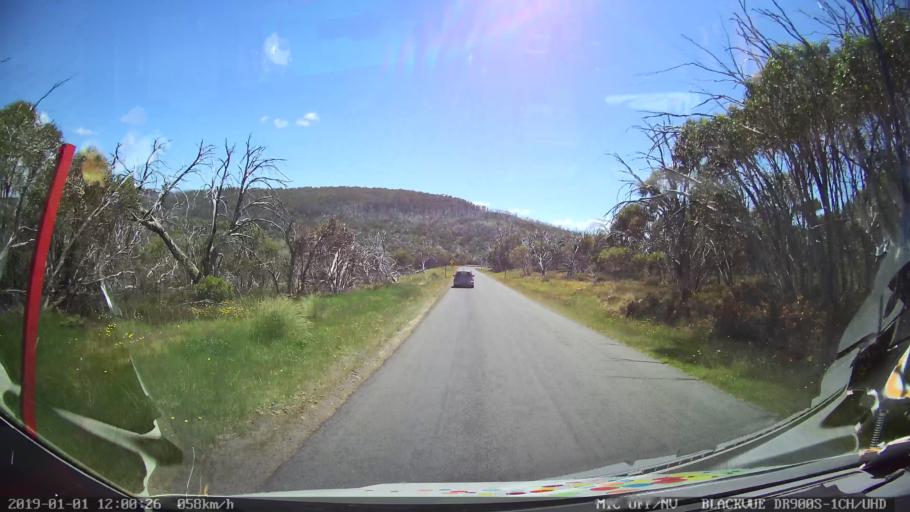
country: AU
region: New South Wales
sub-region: Snowy River
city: Jindabyne
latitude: -35.8849
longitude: 148.4593
